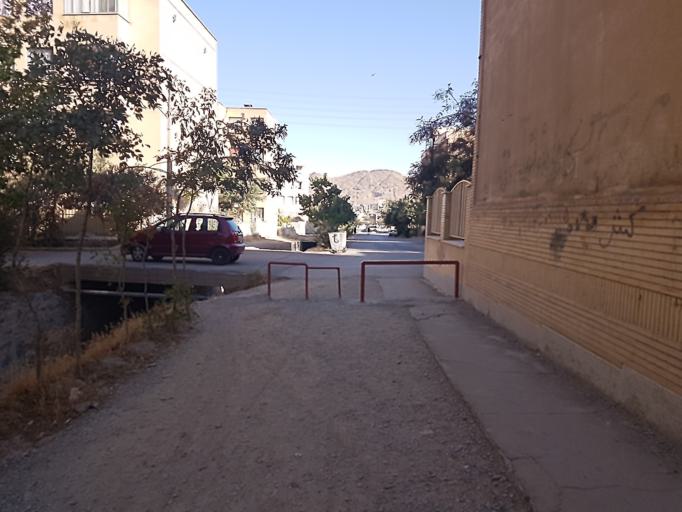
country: IR
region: Markazi
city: Arak
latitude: 34.0694
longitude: 49.6766
